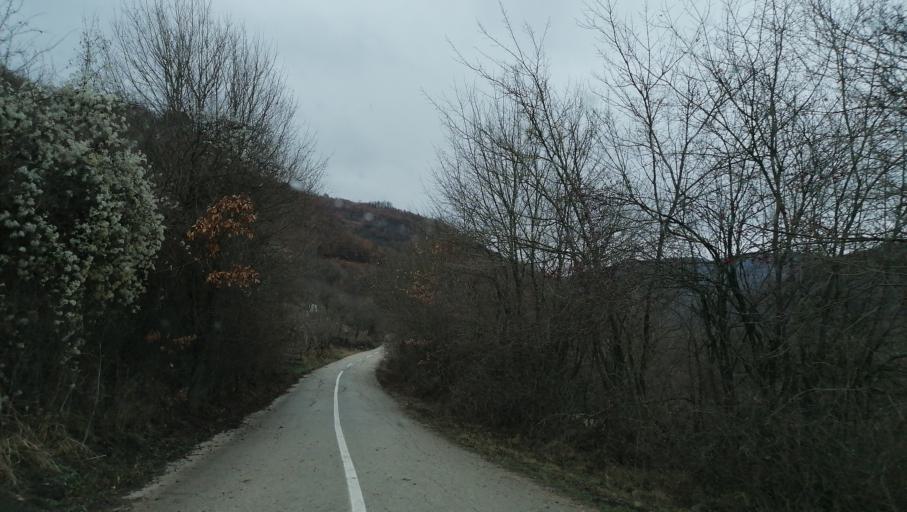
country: RS
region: Central Serbia
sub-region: Pirotski Okrug
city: Dimitrovgrad
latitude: 42.9605
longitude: 22.7826
